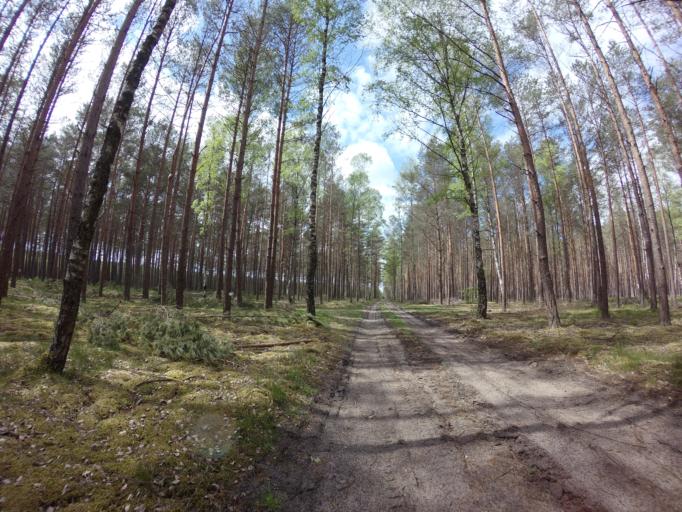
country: PL
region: West Pomeranian Voivodeship
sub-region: Powiat drawski
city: Kalisz Pomorski
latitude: 53.1810
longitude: 15.9846
